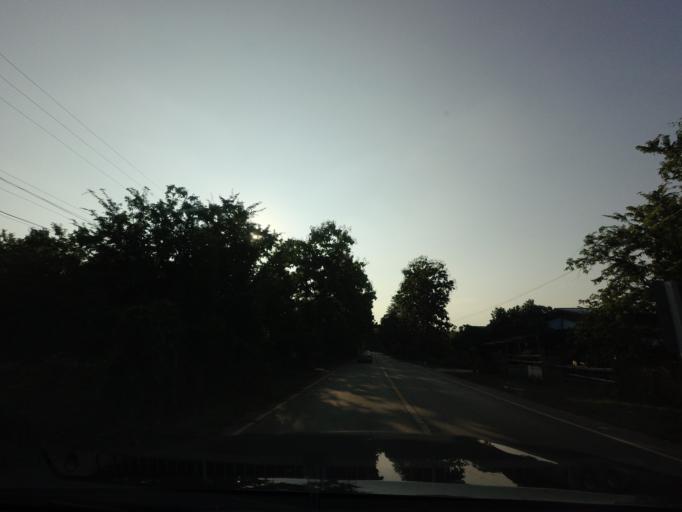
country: TH
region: Nan
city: Na Noi
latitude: 18.3342
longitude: 100.7610
